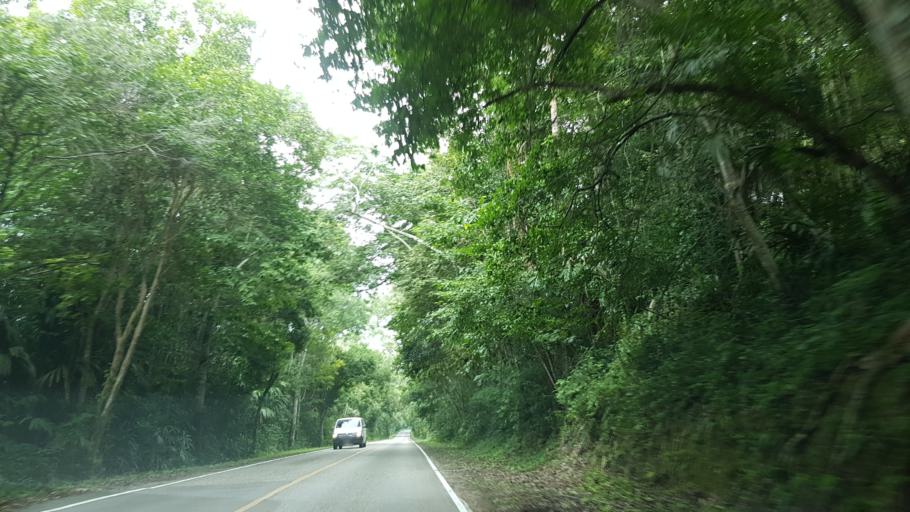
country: GT
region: Peten
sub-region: Municipio de San Jose
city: San Jose
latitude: 17.1710
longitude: -89.6435
